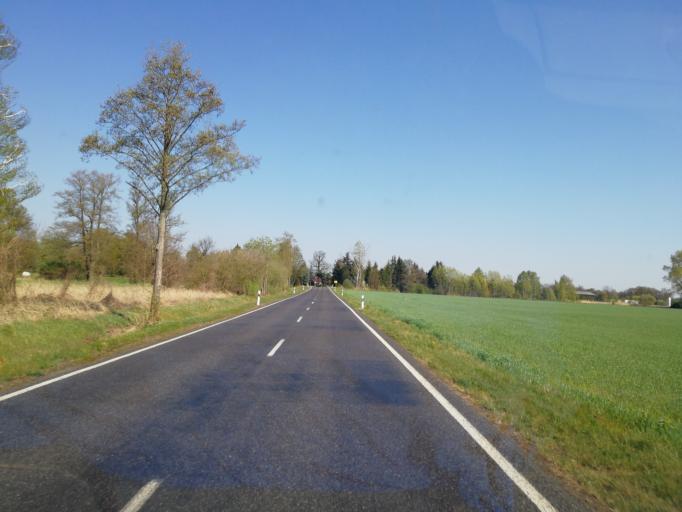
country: DE
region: Brandenburg
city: Calau
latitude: 51.7568
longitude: 13.8594
